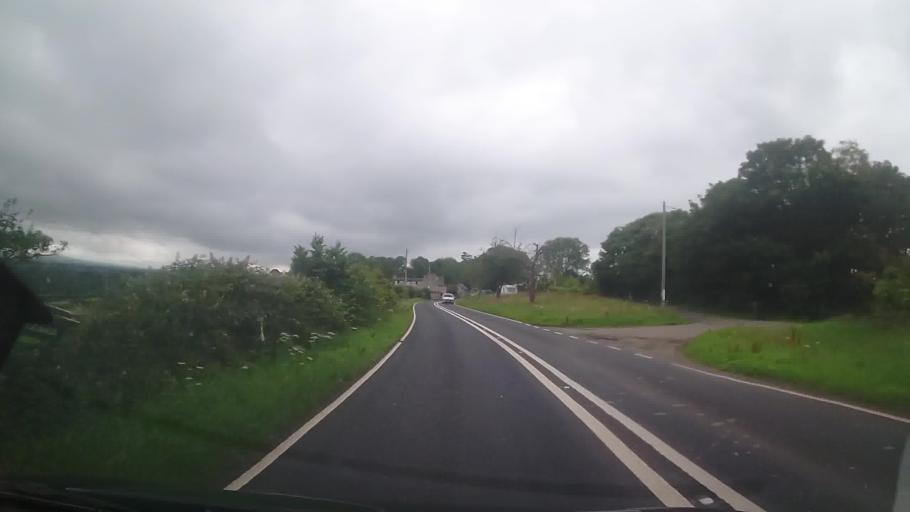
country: GB
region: Wales
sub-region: Anglesey
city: Gaerwen
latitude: 53.1915
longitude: -4.2480
